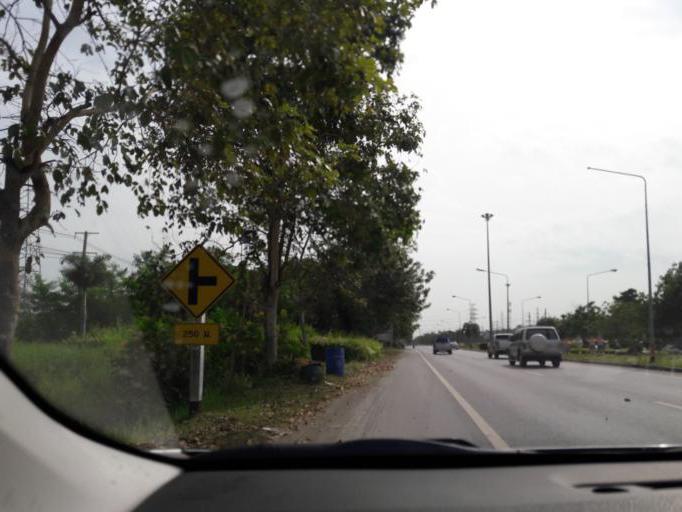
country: TH
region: Ang Thong
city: Ang Thong
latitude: 14.5818
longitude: 100.4604
